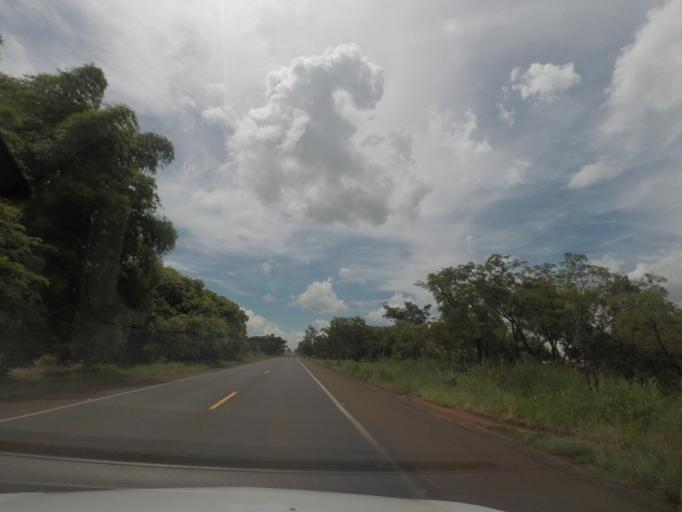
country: BR
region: Sao Paulo
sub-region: Barretos
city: Barretos
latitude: -20.3687
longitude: -48.6462
